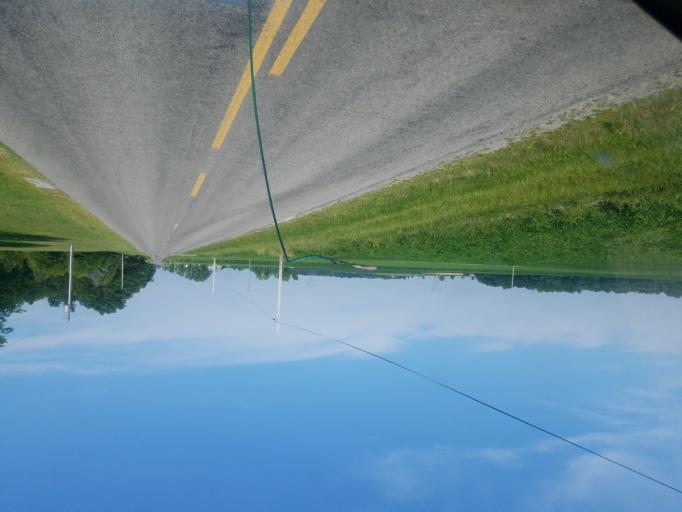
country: US
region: Ohio
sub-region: Shelby County
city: Jackson Center
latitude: 40.4977
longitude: -84.0955
